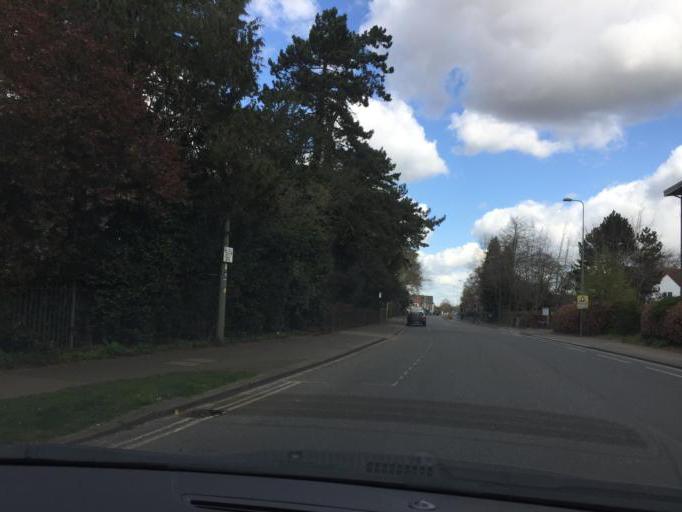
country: GB
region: England
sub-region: Oxfordshire
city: Oxford
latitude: 51.7574
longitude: -1.2356
